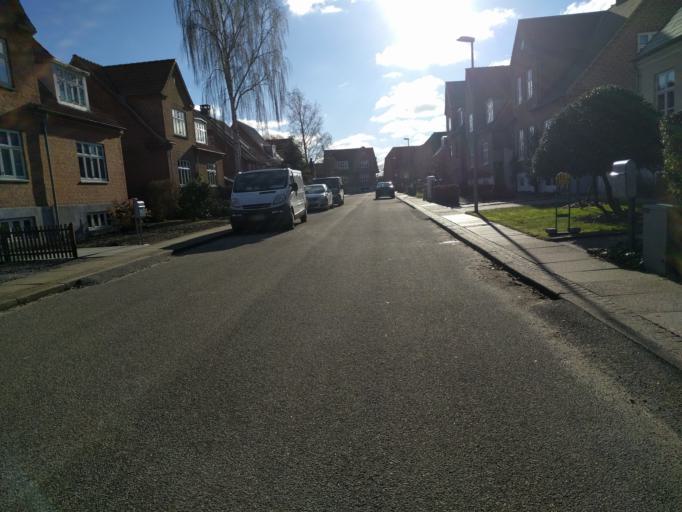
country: DK
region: North Denmark
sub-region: Alborg Kommune
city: Aalborg
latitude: 57.0311
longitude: 9.9191
